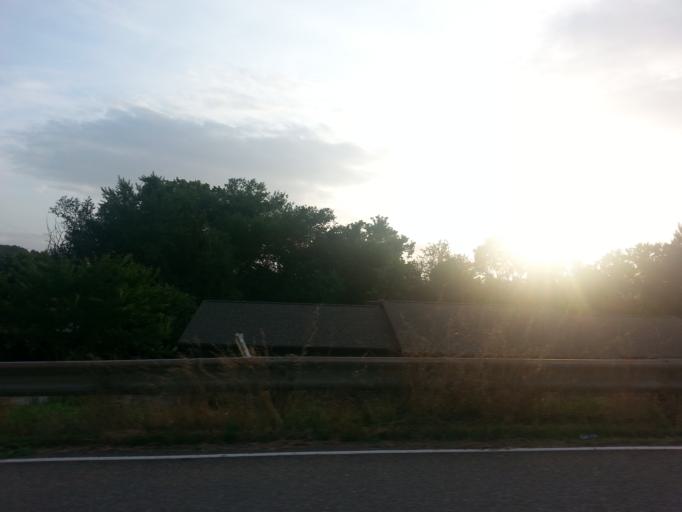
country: US
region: Tennessee
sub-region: Knox County
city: Knoxville
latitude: 35.9819
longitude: -83.8545
